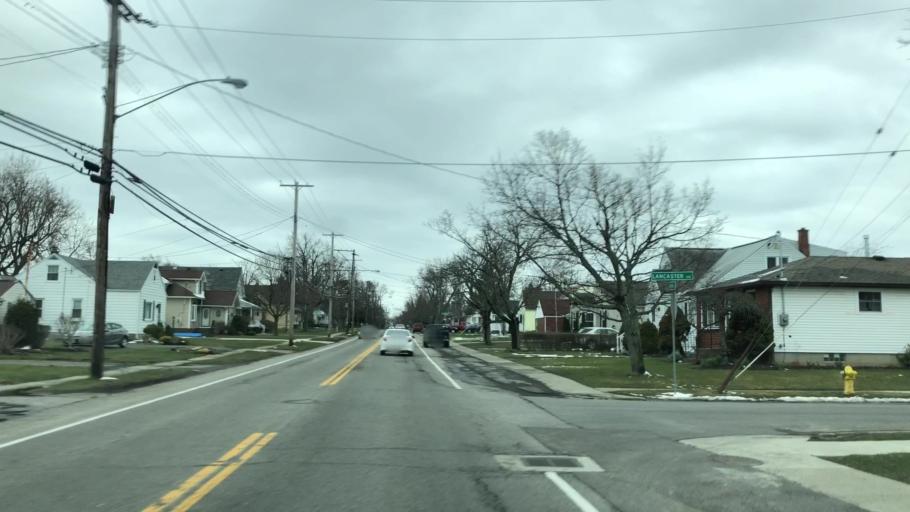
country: US
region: New York
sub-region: Erie County
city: Lancaster
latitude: 42.8900
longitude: -78.6766
